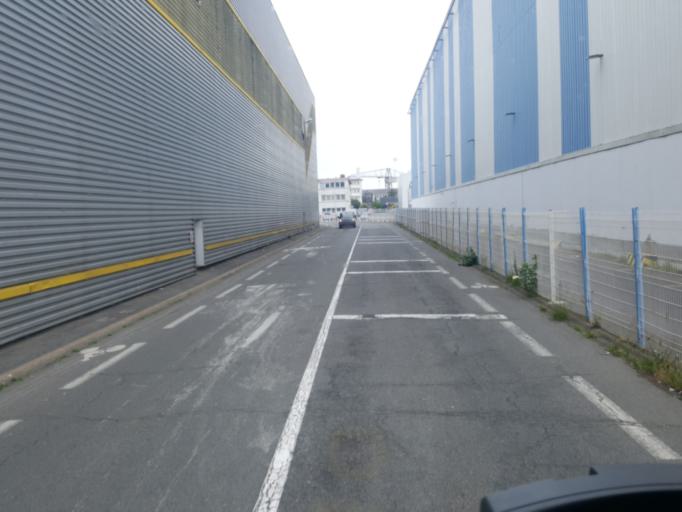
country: FR
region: Pays de la Loire
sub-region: Departement de la Loire-Atlantique
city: Saint-Nazaire
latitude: 47.2837
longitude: -2.1955
